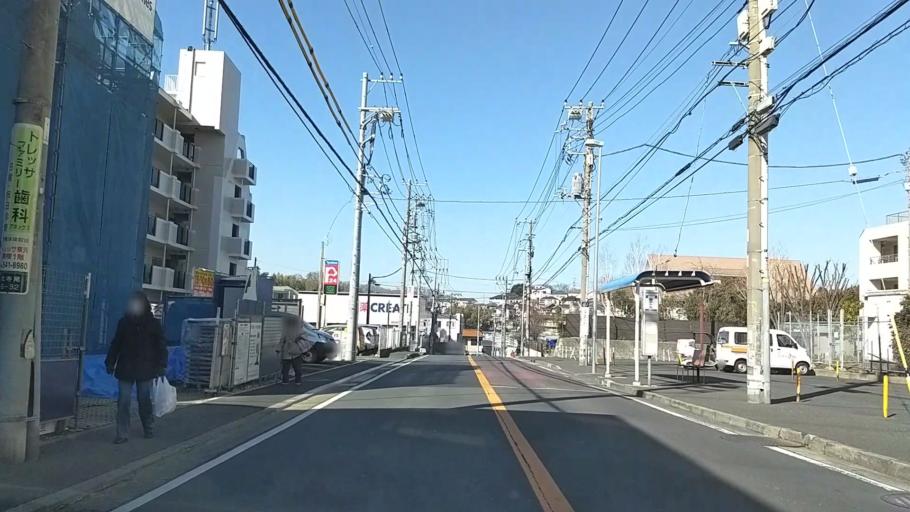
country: JP
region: Kanagawa
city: Yokohama
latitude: 35.5158
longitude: 139.6491
